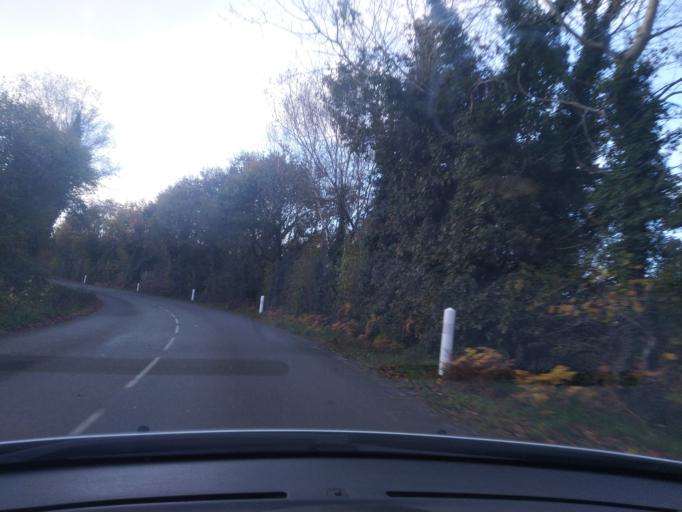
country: FR
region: Brittany
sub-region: Departement du Finistere
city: Plouigneau
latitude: 48.5722
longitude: -3.6413
